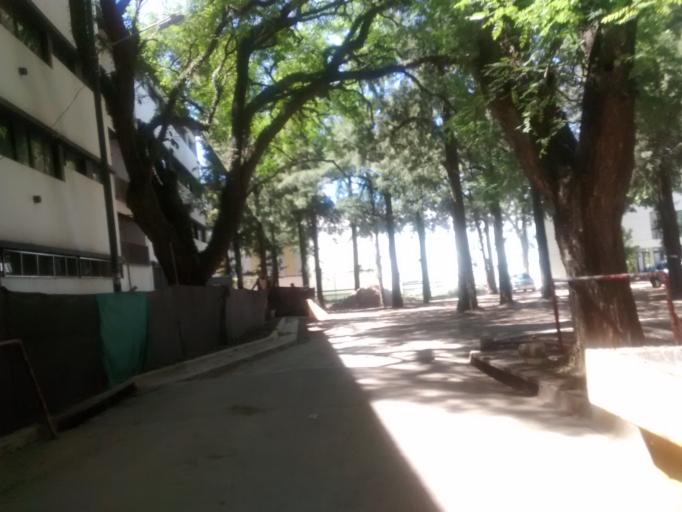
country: AR
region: Buenos Aires
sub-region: Partido de La Plata
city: La Plata
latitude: -34.9055
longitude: -57.9418
